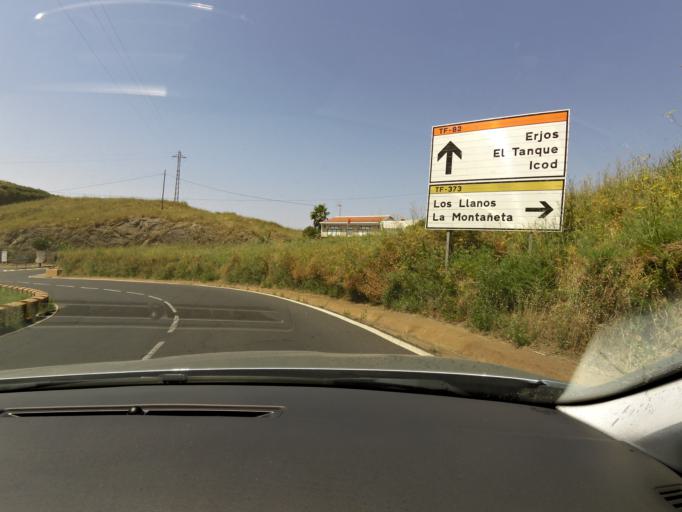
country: ES
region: Canary Islands
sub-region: Provincia de Santa Cruz de Tenerife
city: Santiago del Teide
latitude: 28.3171
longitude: -16.8041
